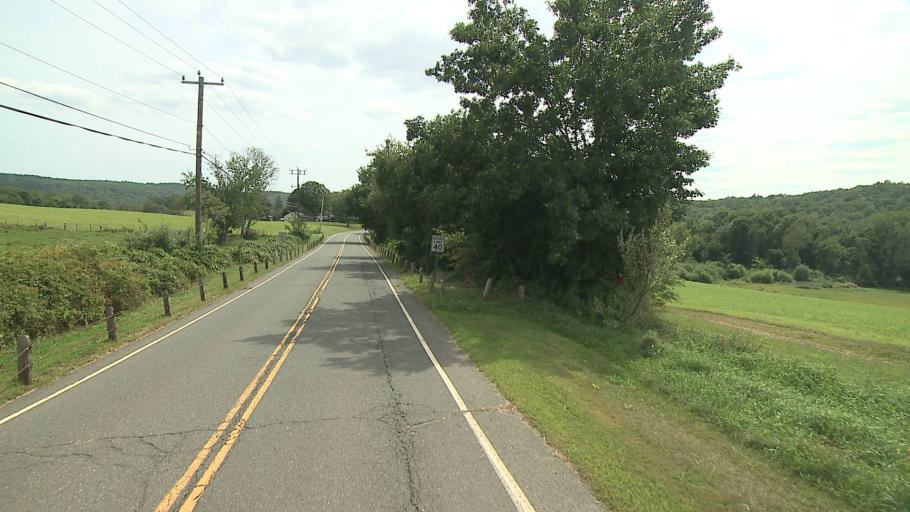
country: US
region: Connecticut
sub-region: Litchfield County
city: Bethlehem Village
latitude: 41.5997
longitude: -73.2399
